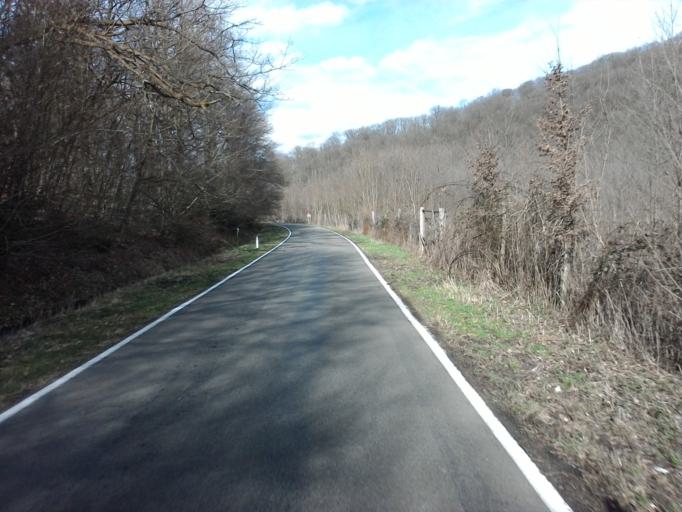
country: BE
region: Wallonia
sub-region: Province du Luxembourg
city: Daverdisse
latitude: 50.0402
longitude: 5.1377
